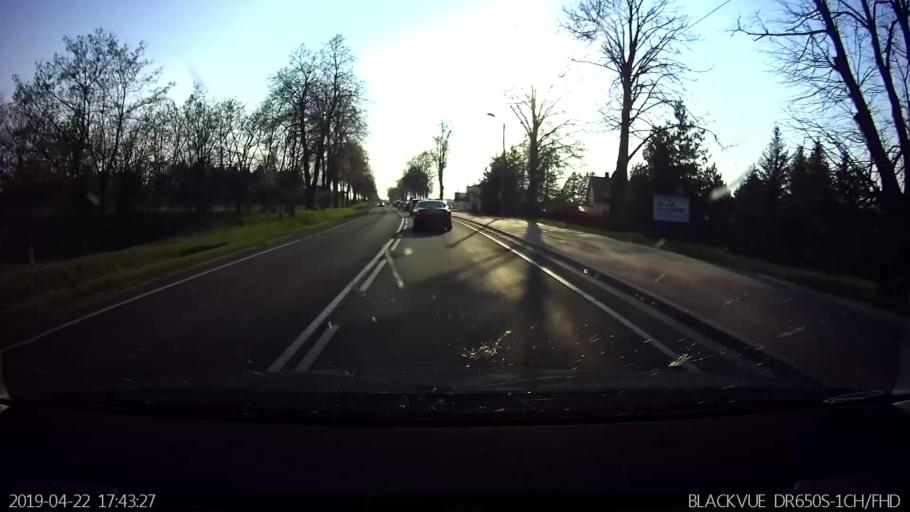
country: PL
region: Masovian Voivodeship
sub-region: Powiat wegrowski
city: Wegrow
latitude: 52.4047
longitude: 22.0613
